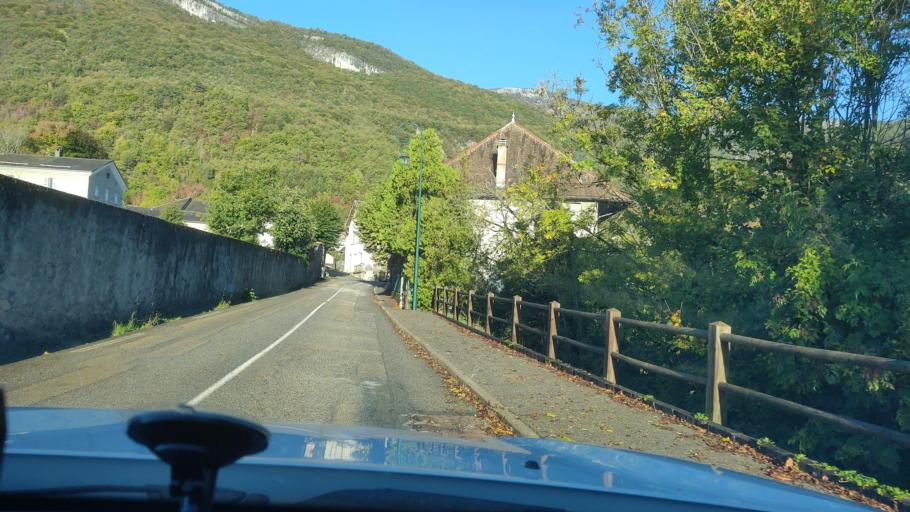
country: FR
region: Rhone-Alpes
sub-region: Departement de la Savoie
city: Cruet
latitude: 45.5273
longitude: 6.0931
